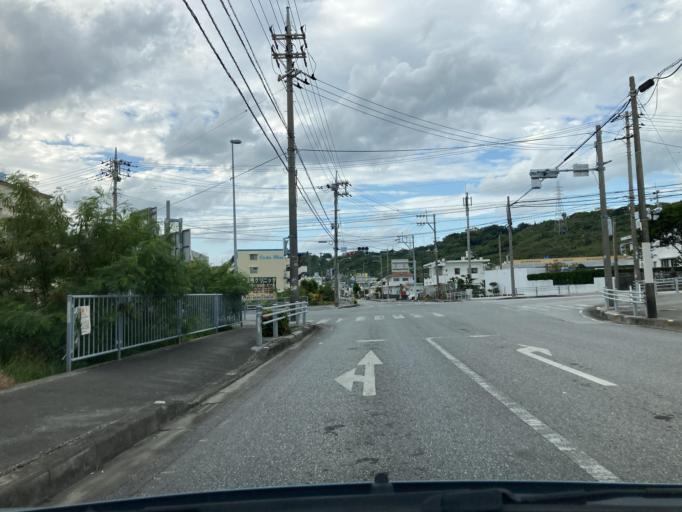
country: JP
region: Okinawa
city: Katsuren-haebaru
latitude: 26.3447
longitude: 127.8675
